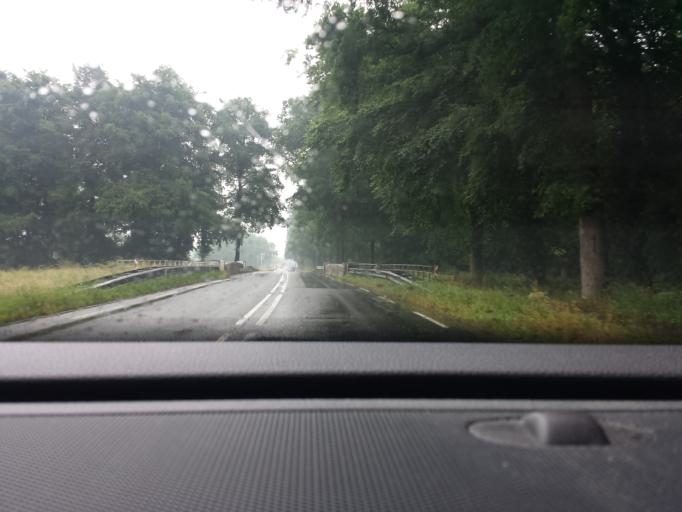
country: NL
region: Gelderland
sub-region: Berkelland
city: Eibergen
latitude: 52.1349
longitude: 6.6840
